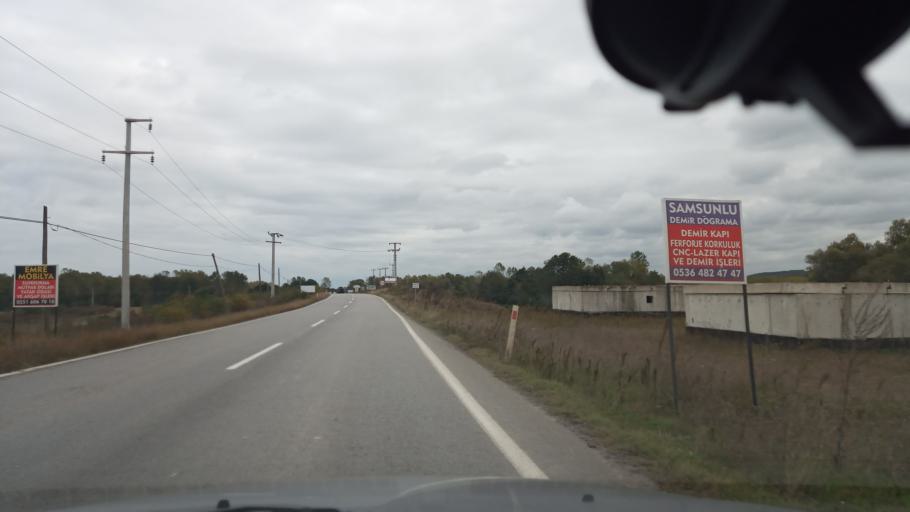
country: TR
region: Sakarya
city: Karasu
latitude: 41.1194
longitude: 30.6041
